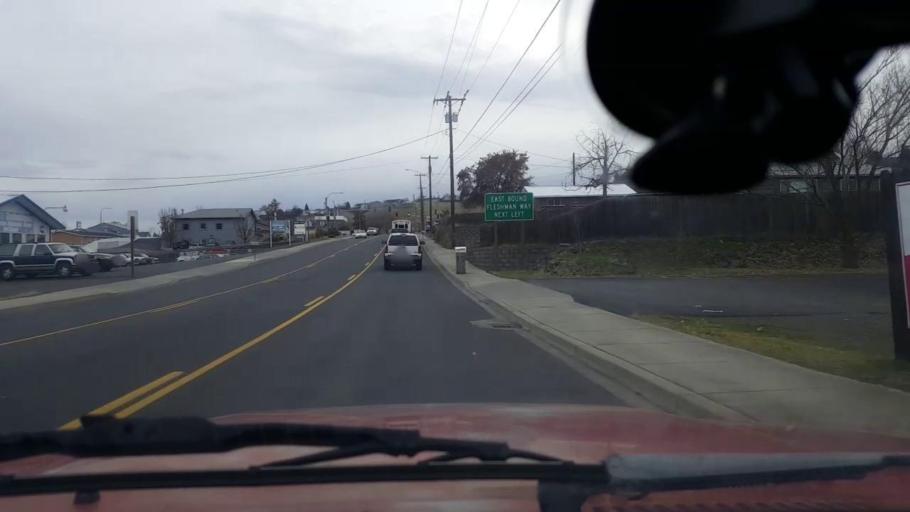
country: US
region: Washington
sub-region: Asotin County
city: West Clarkston-Highland
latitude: 46.4031
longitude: -117.0691
